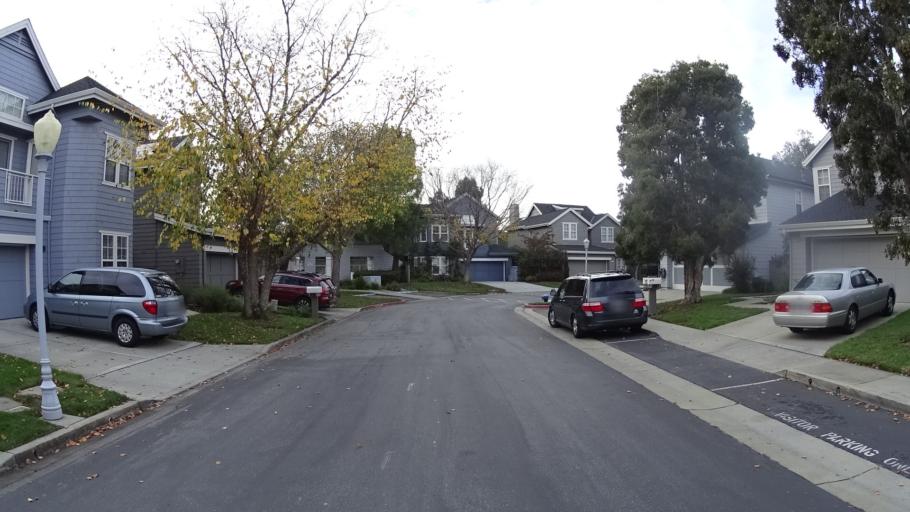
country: US
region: California
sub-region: San Mateo County
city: Redwood Shores
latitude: 37.5331
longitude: -122.2381
